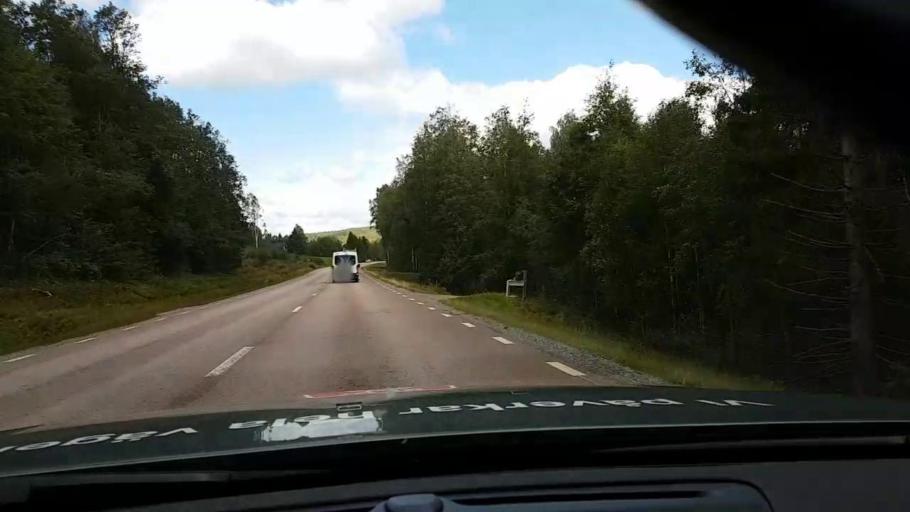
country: SE
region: Vaesternorrland
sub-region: OErnskoeldsviks Kommun
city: Bjasta
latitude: 63.3675
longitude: 18.4451
